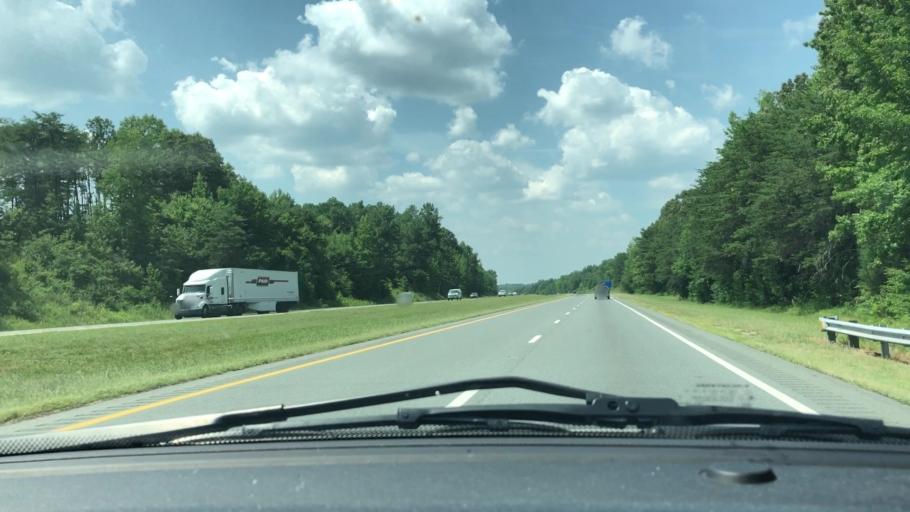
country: US
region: North Carolina
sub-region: Guilford County
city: Forest Oaks
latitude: 35.9477
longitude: -79.6894
